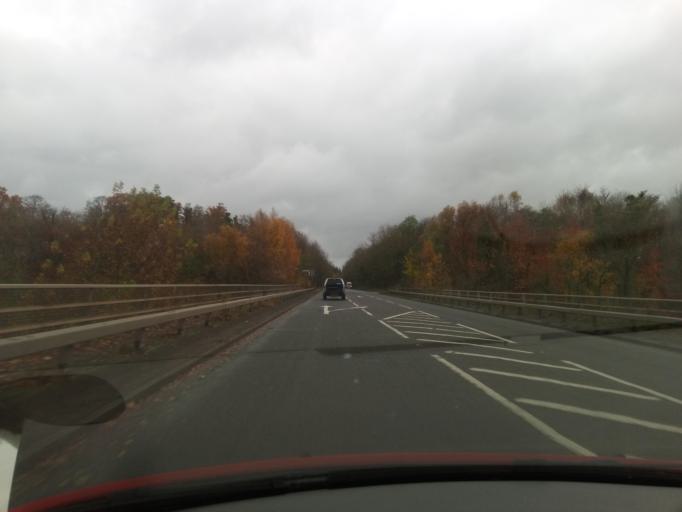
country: GB
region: England
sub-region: County Durham
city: High Etherley
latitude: 54.6713
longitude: -1.7764
